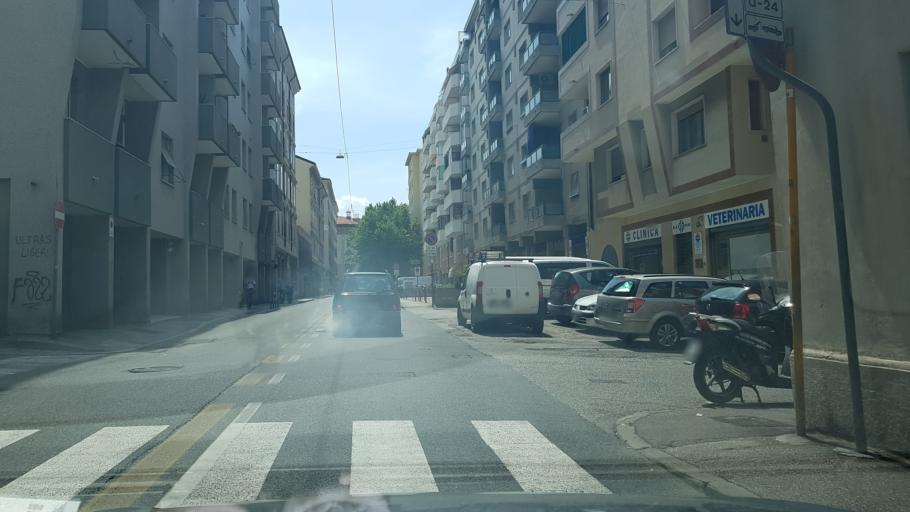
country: IT
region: Friuli Venezia Giulia
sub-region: Provincia di Trieste
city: Trieste
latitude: 45.6451
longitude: 13.7860
